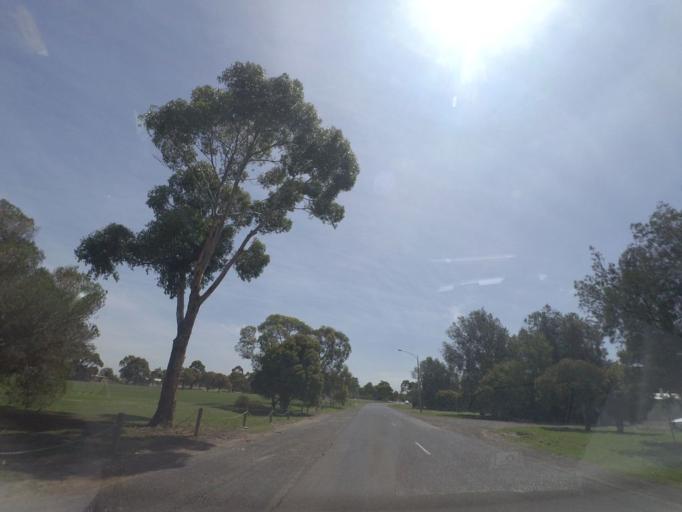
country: AU
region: Victoria
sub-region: Brimbank
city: Keilor Park
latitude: -37.7138
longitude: 144.8522
